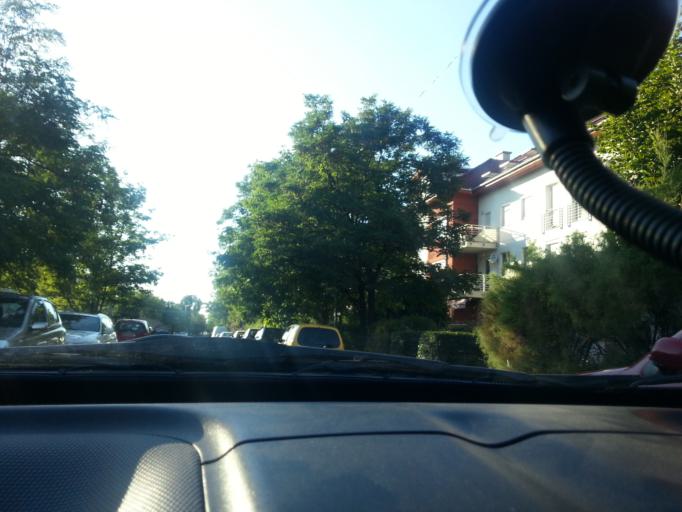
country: HU
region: Pest
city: Gyal
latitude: 47.4194
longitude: 19.2086
